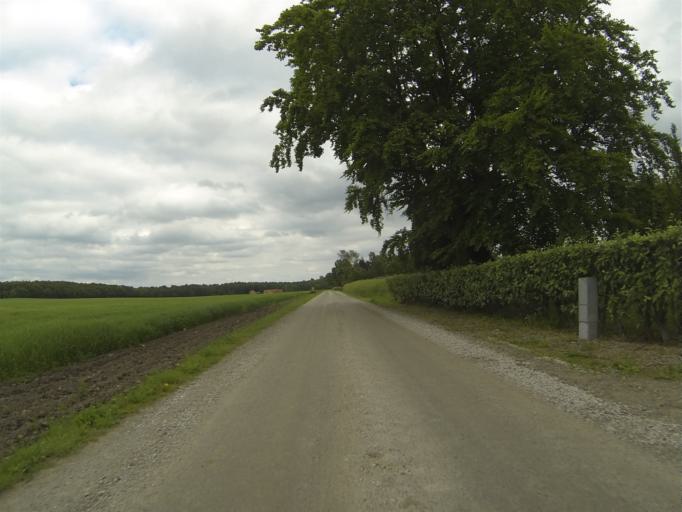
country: SE
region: Skane
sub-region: Lunds Kommun
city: Lund
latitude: 55.7306
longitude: 13.2826
